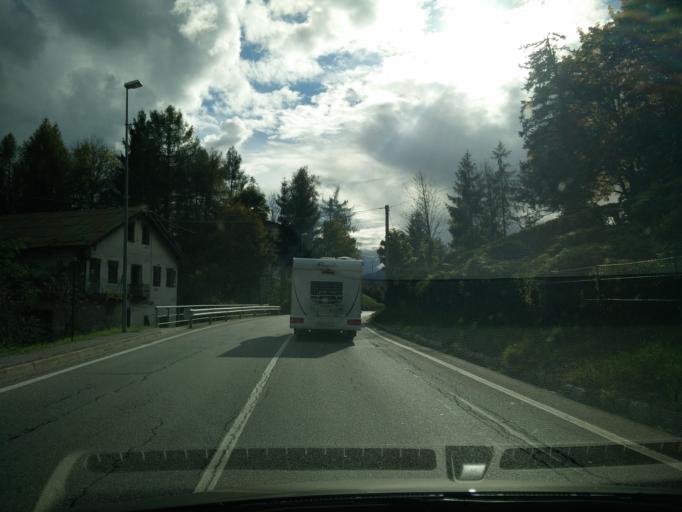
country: IT
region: Veneto
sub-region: Provincia di Belluno
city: Domegge di Cadore
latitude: 46.4541
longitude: 12.4050
